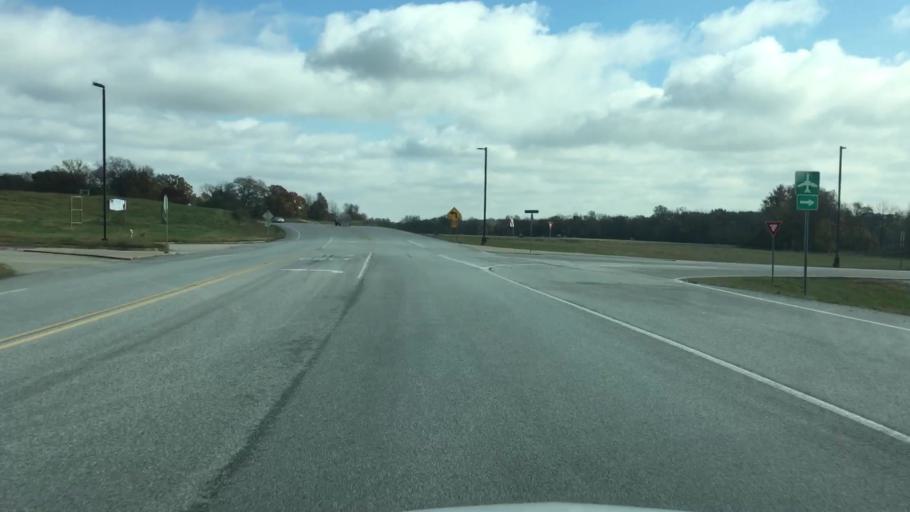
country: US
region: Arkansas
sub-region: Benton County
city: Centerton
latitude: 36.3006
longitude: -94.3075
